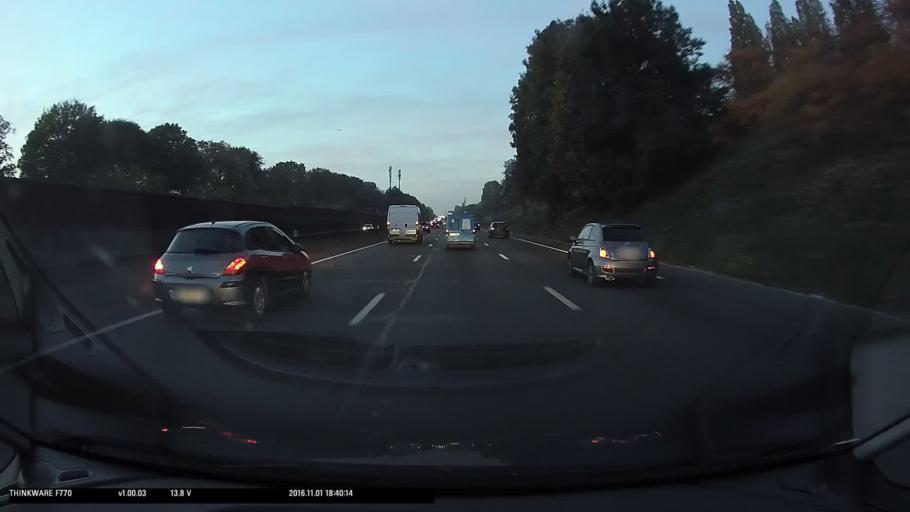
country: FR
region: Ile-de-France
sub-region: Departement de l'Essonne
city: Villemoisson-sur-Orge
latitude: 48.6827
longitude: 2.3296
